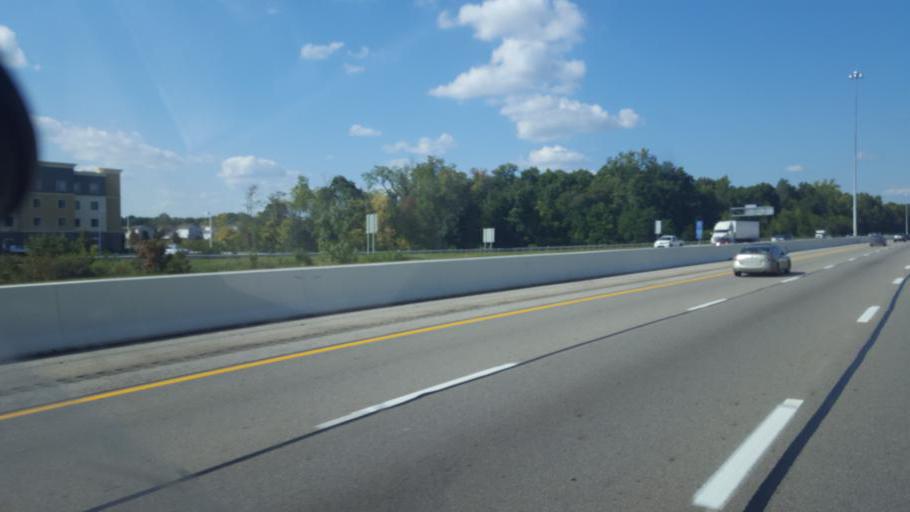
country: US
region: Ohio
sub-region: Franklin County
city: Westerville
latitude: 40.1501
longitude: -82.9702
